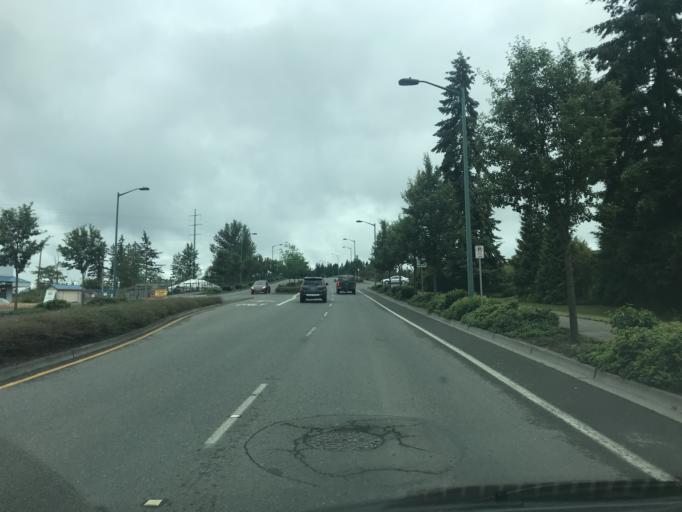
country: US
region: Washington
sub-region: King County
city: Covington
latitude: 47.3533
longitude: -122.1220
